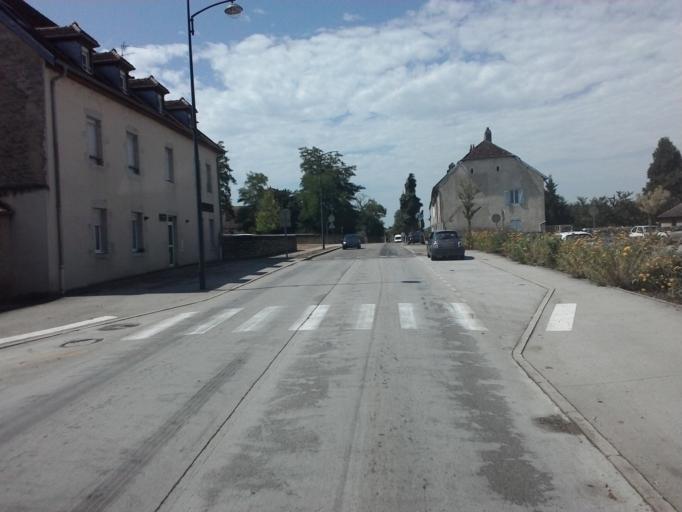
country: FR
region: Franche-Comte
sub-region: Departement du Jura
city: Cousance
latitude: 46.5748
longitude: 5.4363
